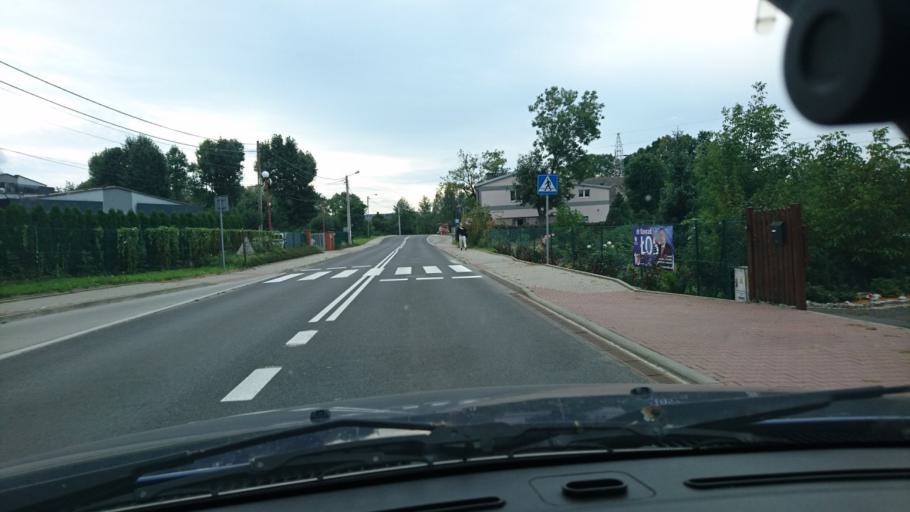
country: PL
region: Silesian Voivodeship
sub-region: Powiat bielski
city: Mazancowice
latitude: 49.8216
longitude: 18.9832
